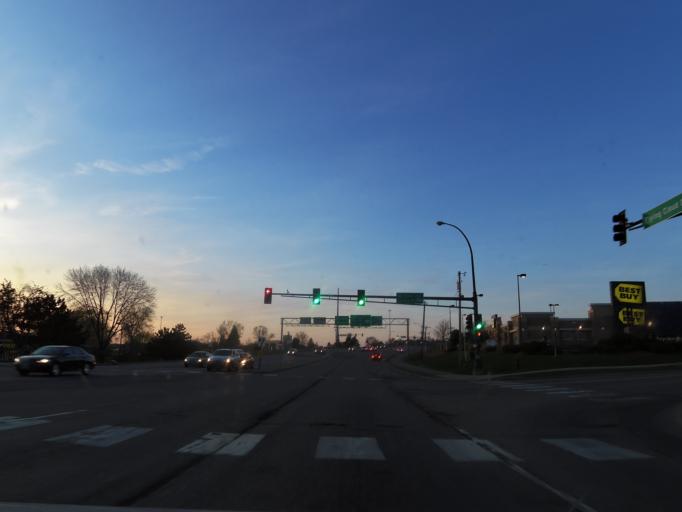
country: US
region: Minnesota
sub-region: Hennepin County
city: Eden Prairie
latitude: 44.8596
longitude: -93.4257
